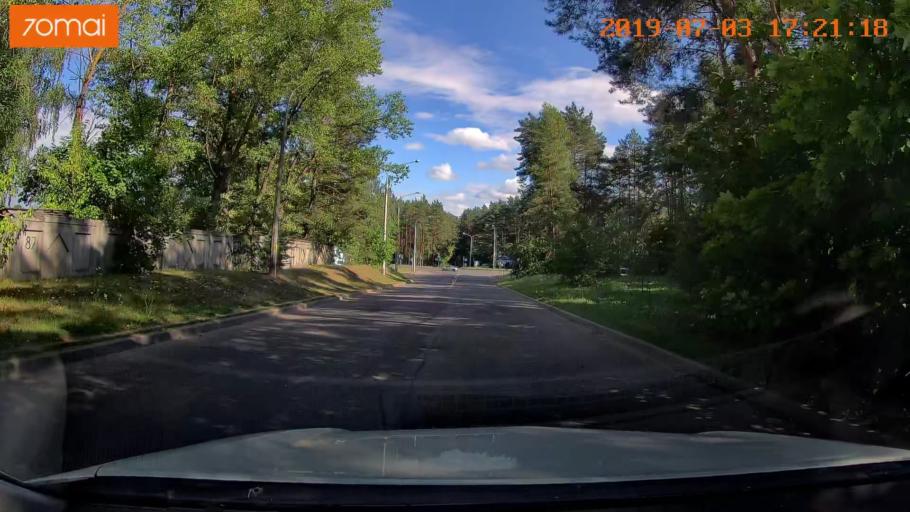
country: BY
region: Minsk
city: Vyaliki Trastsyanets
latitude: 53.9029
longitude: 27.6808
